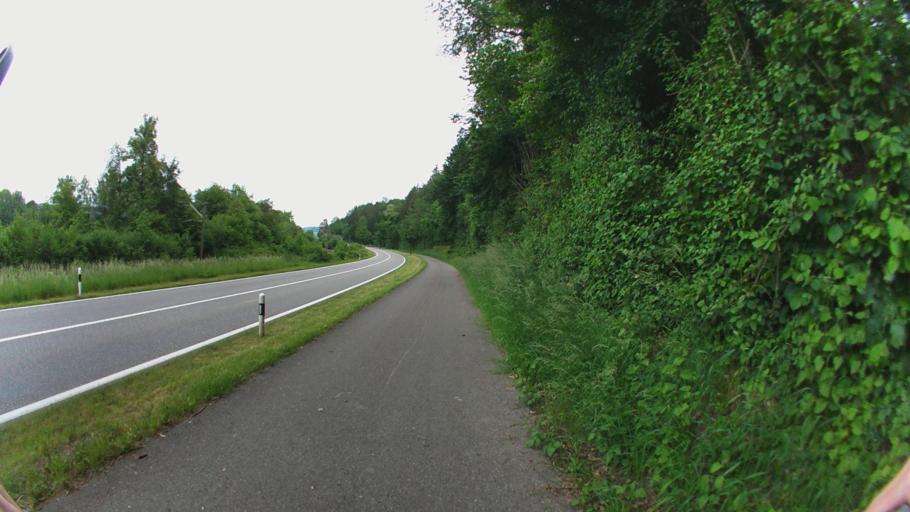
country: CH
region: Aargau
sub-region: Bezirk Zurzach
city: Koblenz
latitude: 47.6089
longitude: 8.2622
